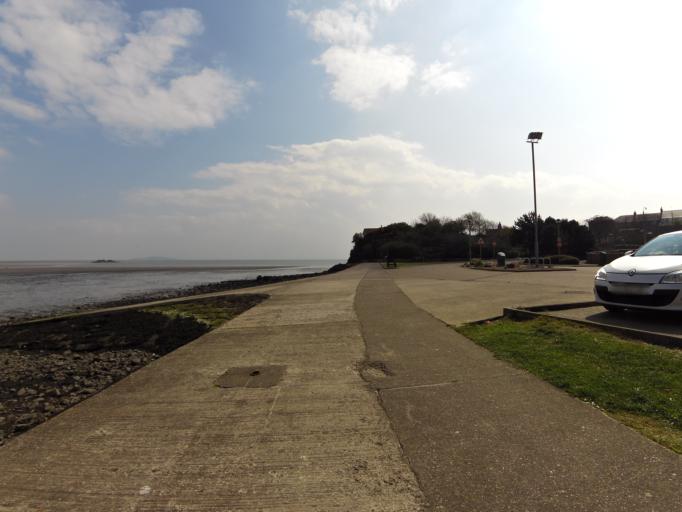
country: GB
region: Scotland
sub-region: Fife
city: Burntisland
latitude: 56.0597
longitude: -3.2243
